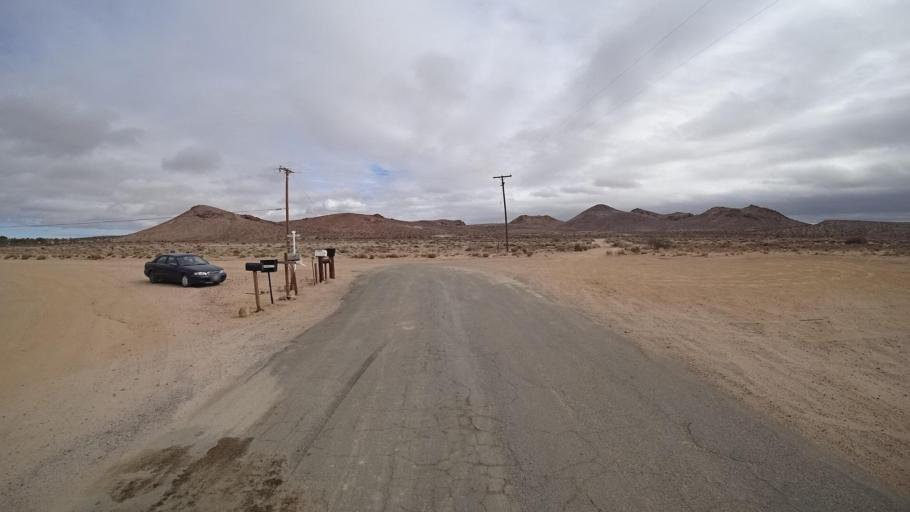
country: US
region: California
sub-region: Kern County
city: Rosamond
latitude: 34.8931
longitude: -118.2036
